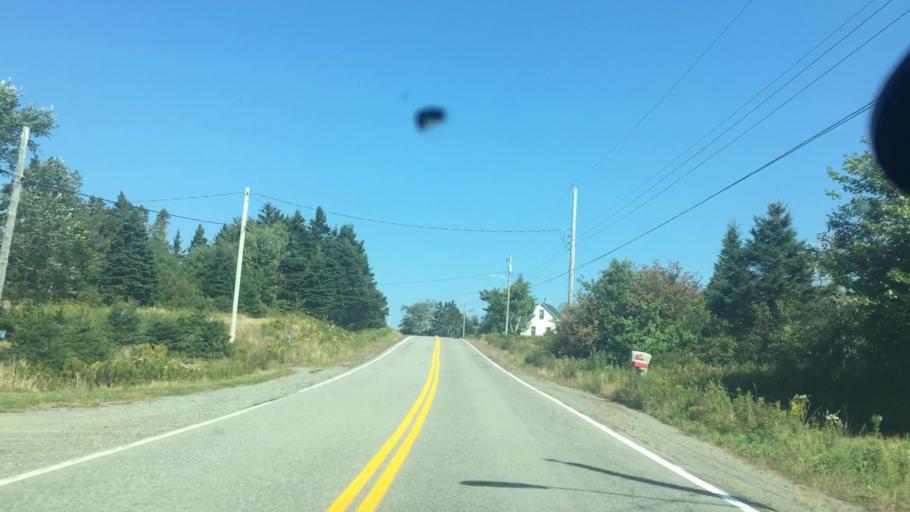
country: CA
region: Nova Scotia
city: New Glasgow
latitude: 44.9124
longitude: -62.3843
